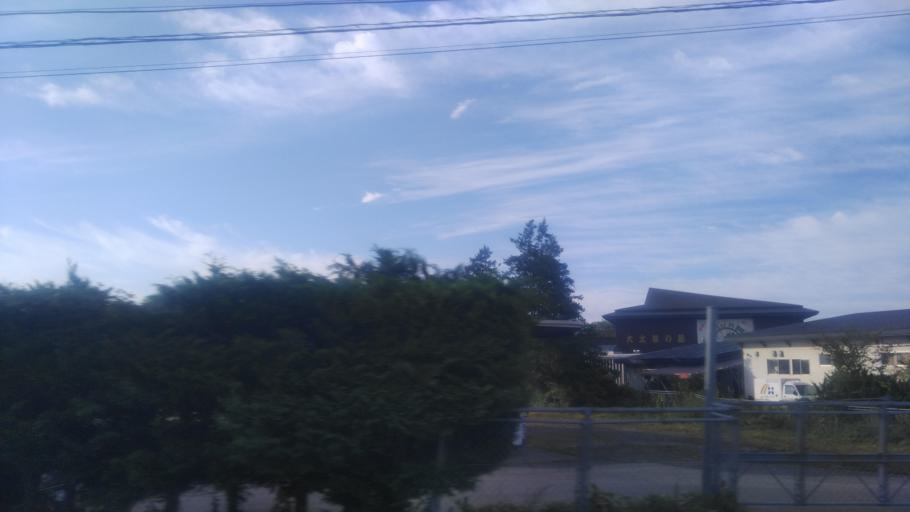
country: JP
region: Akita
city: Takanosu
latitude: 40.2521
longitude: 140.3765
